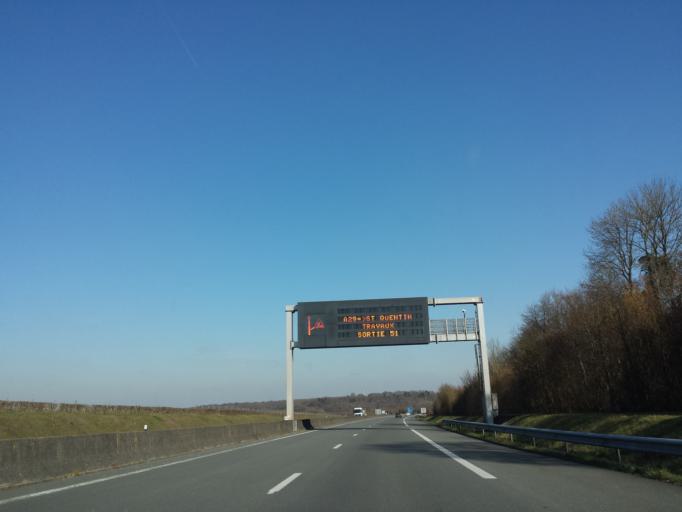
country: FR
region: Picardie
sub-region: Departement de la Somme
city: Saleux
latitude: 49.8222
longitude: 2.2480
